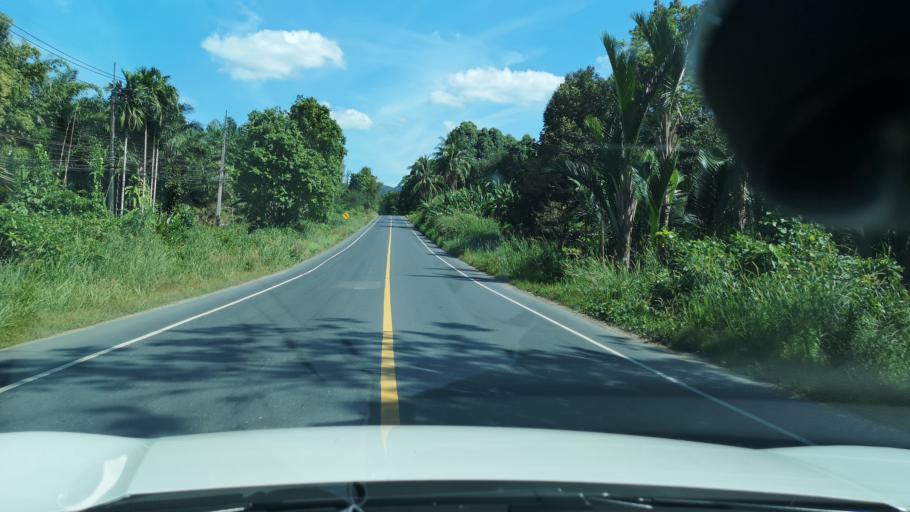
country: TH
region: Phangnga
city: Phang Nga
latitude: 8.5339
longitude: 98.5038
